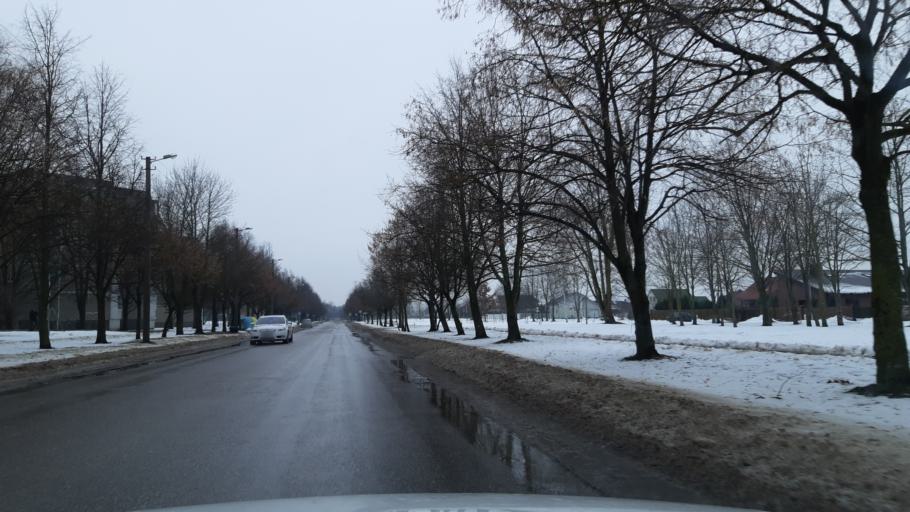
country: LT
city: Vilkaviskis
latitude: 54.6568
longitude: 23.0293
